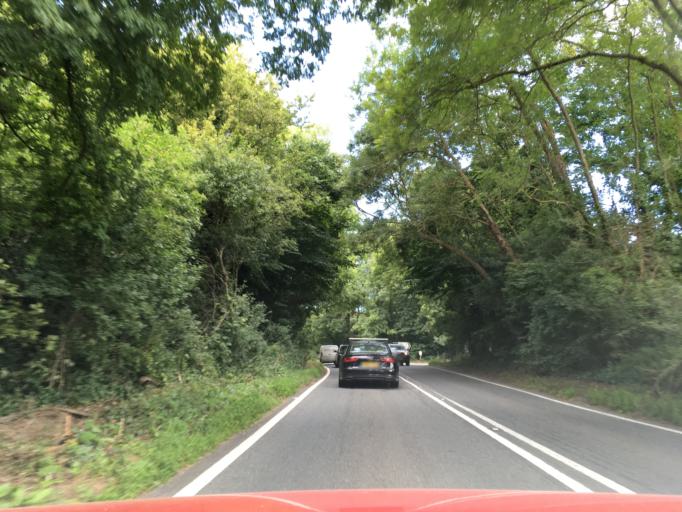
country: GB
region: England
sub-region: Somerset
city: Yeovil
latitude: 50.9147
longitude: -2.6286
